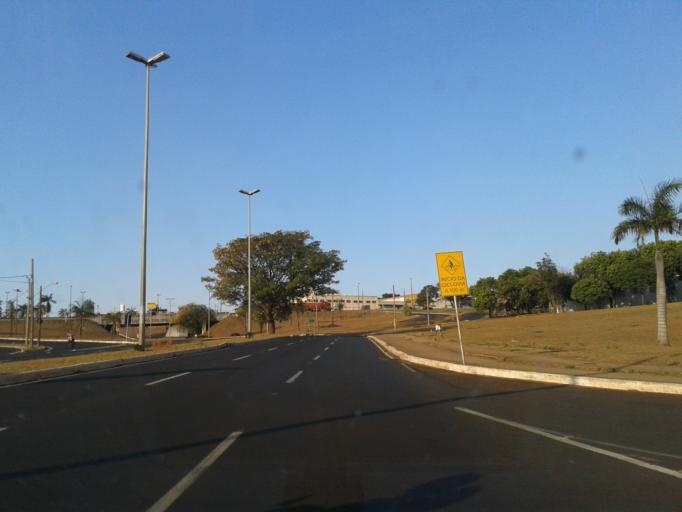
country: BR
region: Minas Gerais
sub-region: Uberlandia
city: Uberlandia
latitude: -18.8949
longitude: -48.2527
